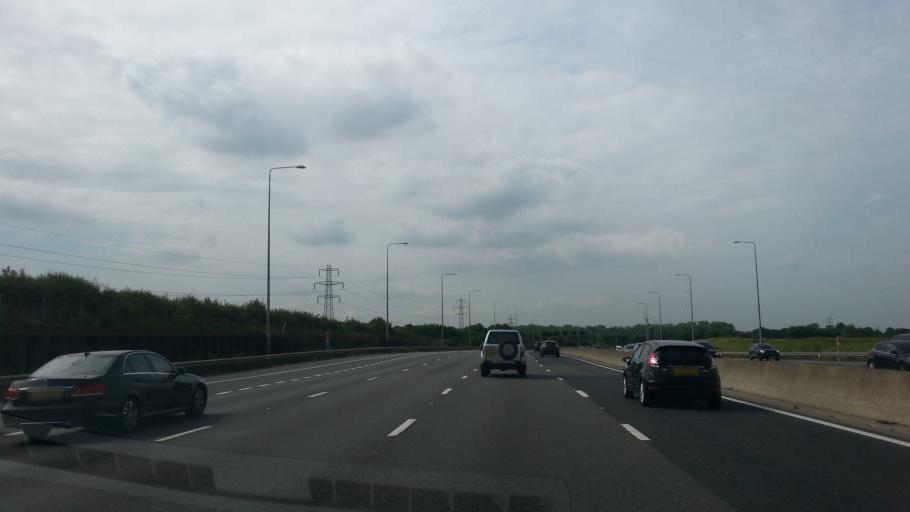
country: GB
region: England
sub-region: Hertfordshire
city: Shenley AV
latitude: 51.7131
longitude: -0.2877
